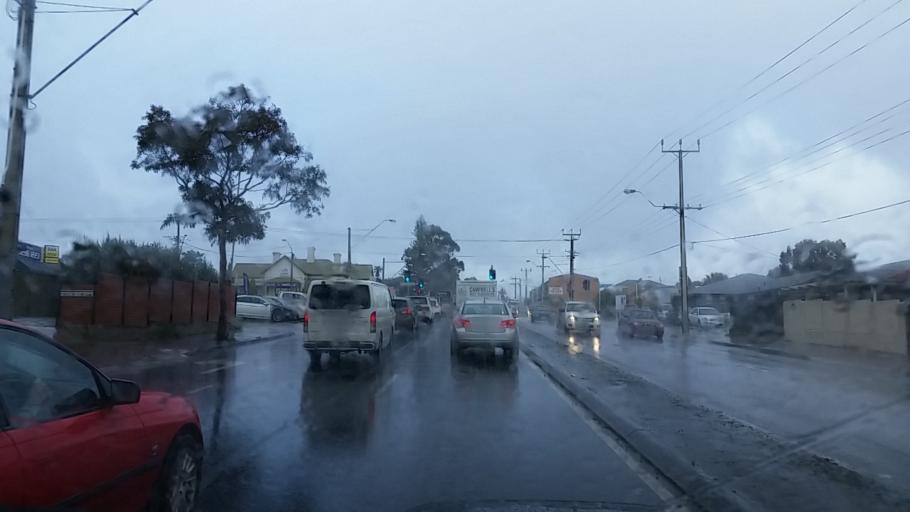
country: AU
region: South Australia
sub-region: Adelaide Hills
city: Seacliff
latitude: -35.0295
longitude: 138.5239
